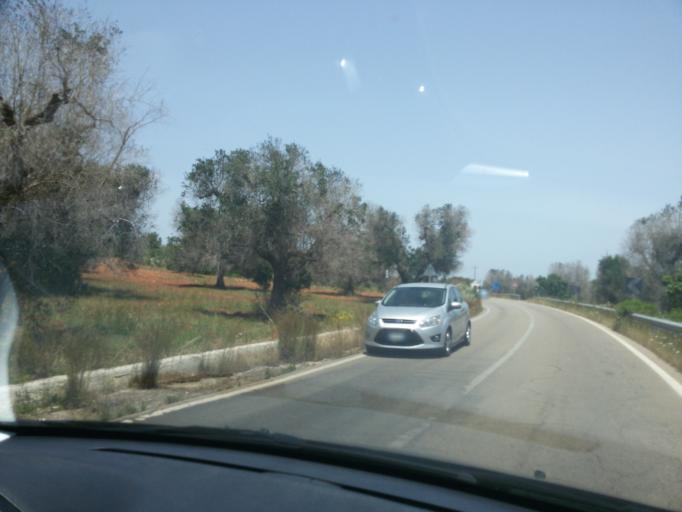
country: IT
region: Apulia
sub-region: Provincia di Lecce
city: Porto Cesareo
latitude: 40.2977
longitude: 17.9185
